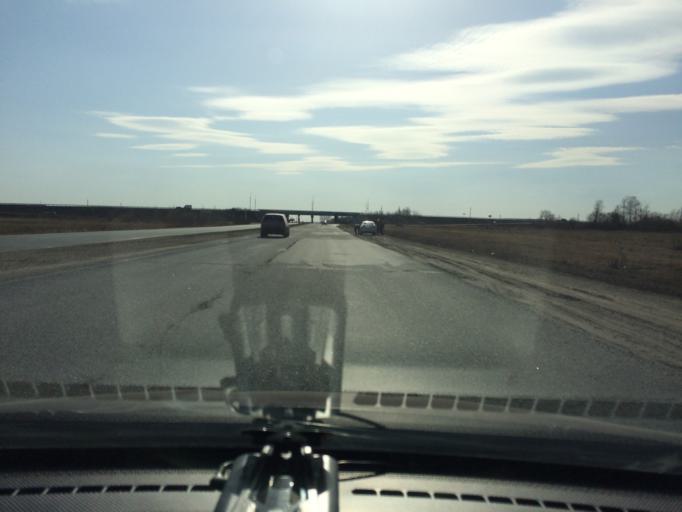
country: RU
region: Mariy-El
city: Yoshkar-Ola
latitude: 56.6816
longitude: 48.0279
